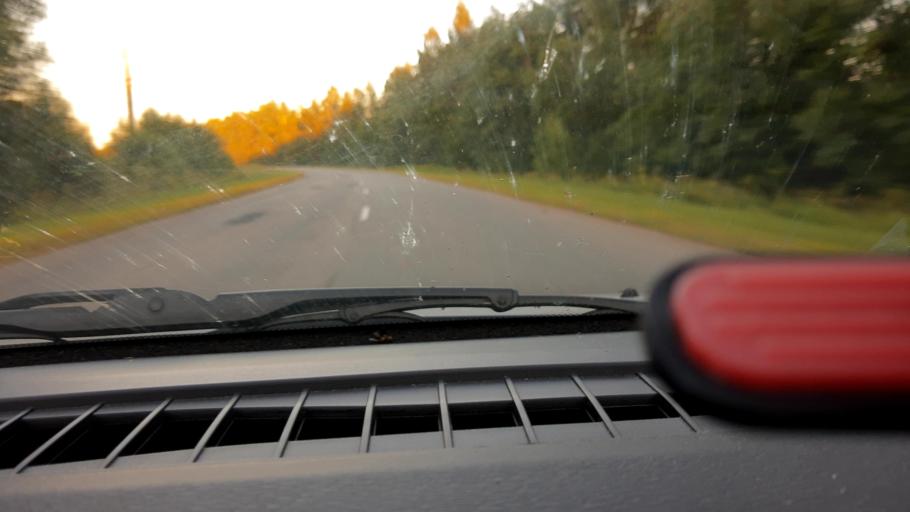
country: RU
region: Nizjnij Novgorod
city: Prudy
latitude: 57.3638
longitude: 46.1824
